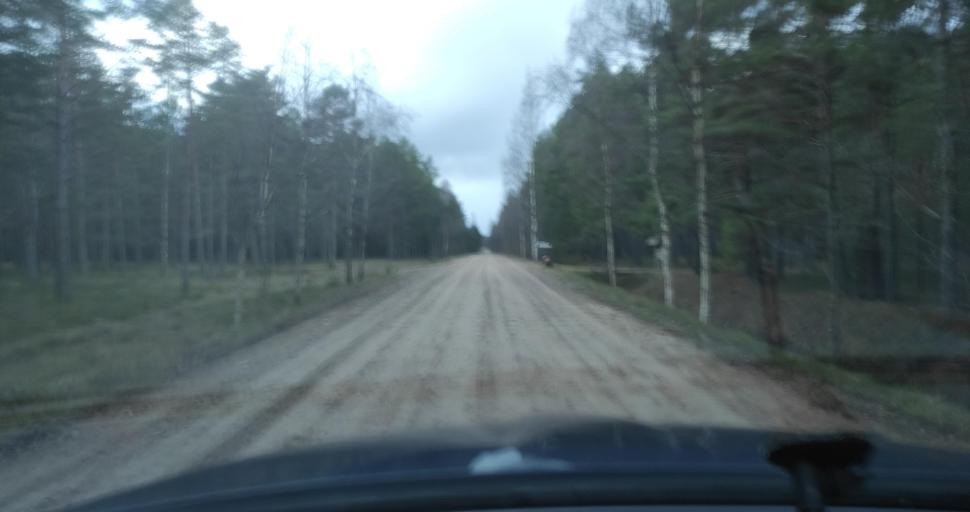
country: LV
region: Pavilostas
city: Pavilosta
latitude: 56.8525
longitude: 21.1167
